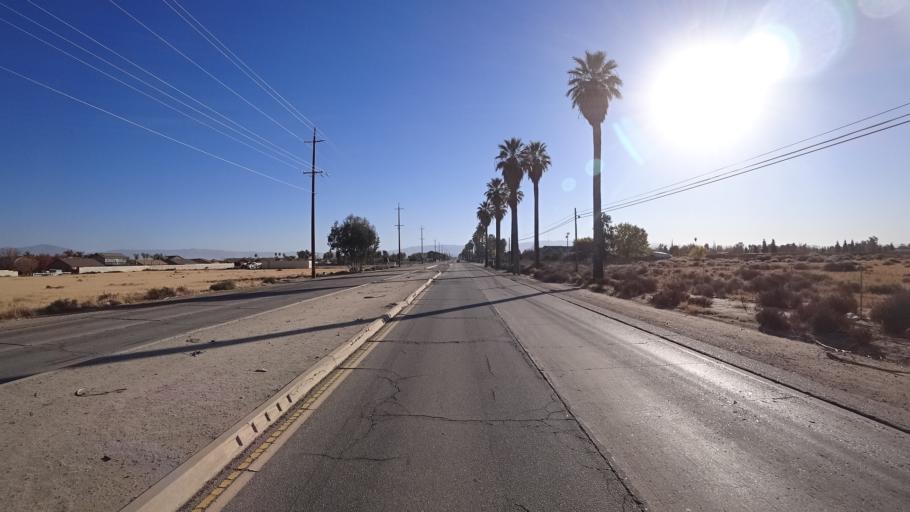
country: US
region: California
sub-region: Kern County
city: Greenfield
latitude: 35.2799
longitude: -119.0031
